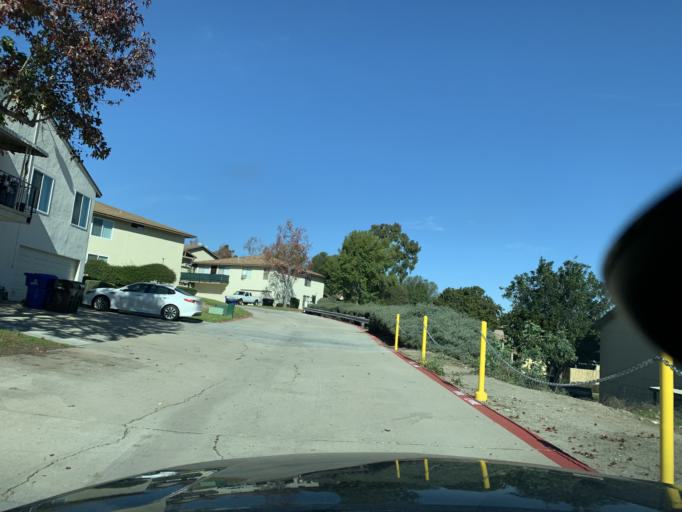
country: US
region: California
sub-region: San Diego County
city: Poway
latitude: 32.9668
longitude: -117.0960
